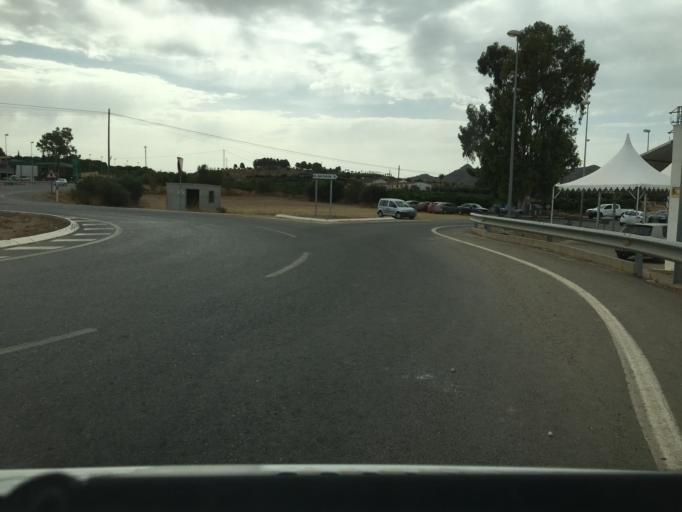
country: ES
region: Andalusia
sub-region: Provincia de Almeria
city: Huercal-Overa
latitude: 37.4170
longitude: -1.8784
